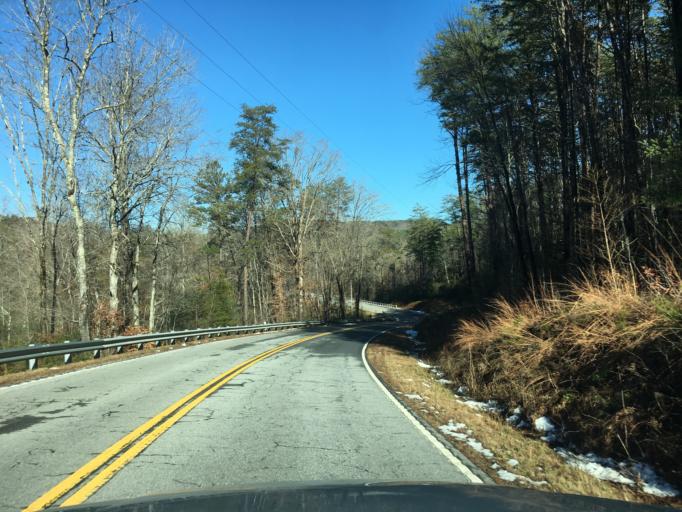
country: US
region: South Carolina
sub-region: Oconee County
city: Walhalla
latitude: 34.9113
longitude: -82.9863
